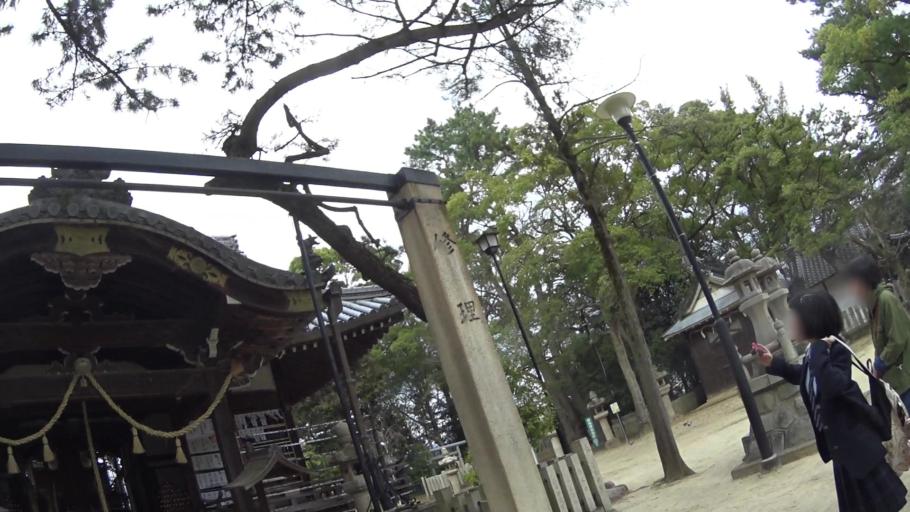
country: JP
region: Hyogo
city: Itami
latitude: 34.7850
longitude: 135.4155
